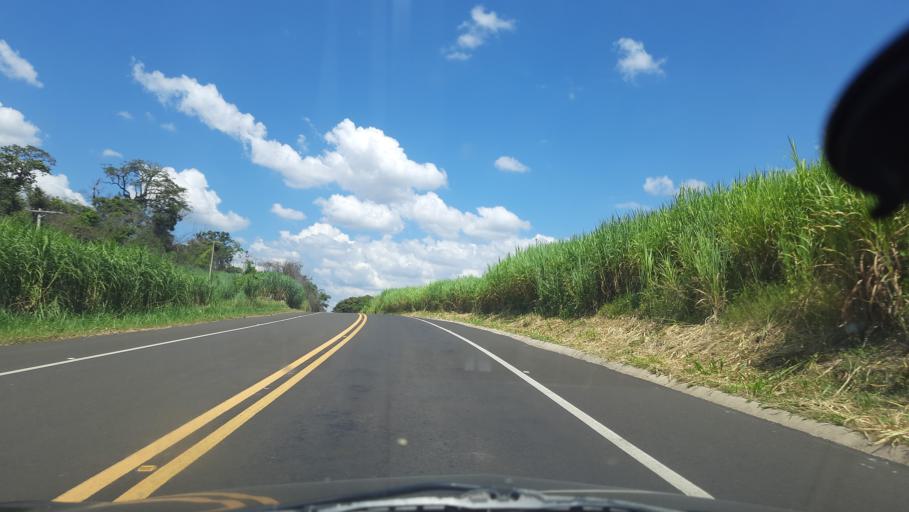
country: BR
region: Sao Paulo
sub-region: Sao Jose Do Rio Pardo
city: Sao Jose do Rio Pardo
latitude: -21.5926
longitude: -46.9926
